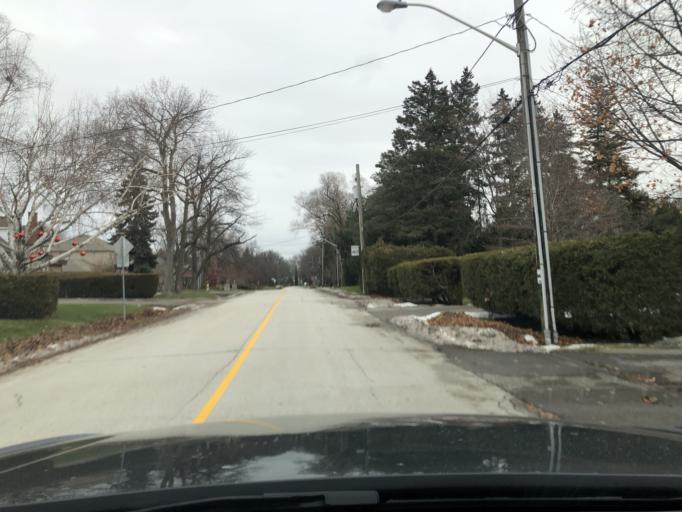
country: CA
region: Ontario
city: Etobicoke
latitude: 43.6947
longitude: -79.5284
